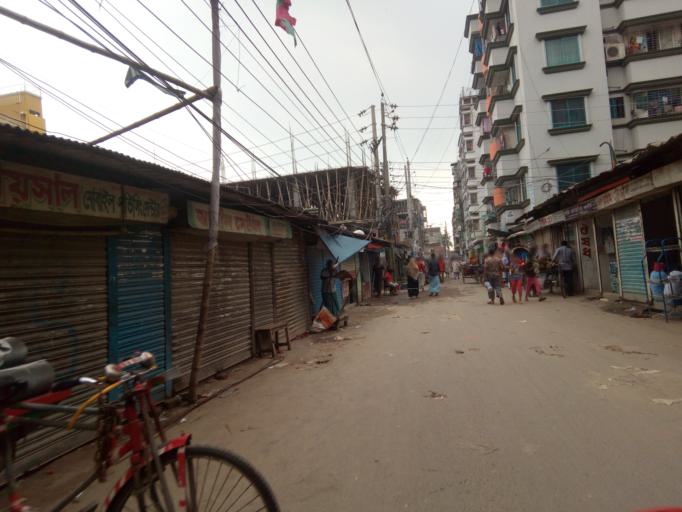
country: BD
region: Dhaka
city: Azimpur
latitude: 23.7170
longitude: 90.3639
